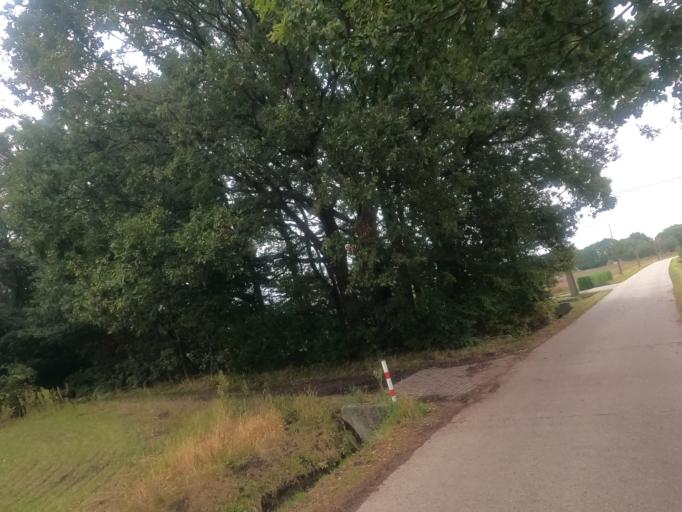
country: BE
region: Flanders
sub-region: Provincie Antwerpen
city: Nijlen
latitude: 51.1465
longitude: 4.6554
